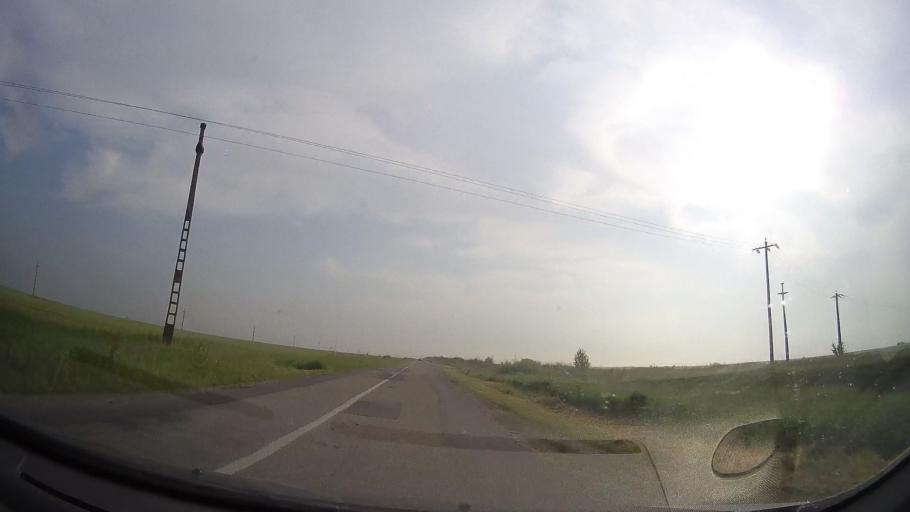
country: RO
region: Timis
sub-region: Comuna Giulvaz
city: Giulvaz
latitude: 45.5643
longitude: 20.9994
